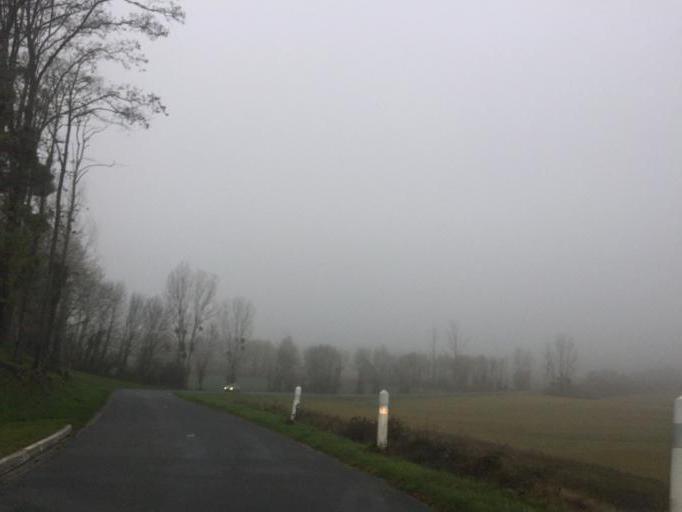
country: FR
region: Rhone-Alpes
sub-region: Departement de l'Ain
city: Tramoyes
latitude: 45.8802
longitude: 4.9708
